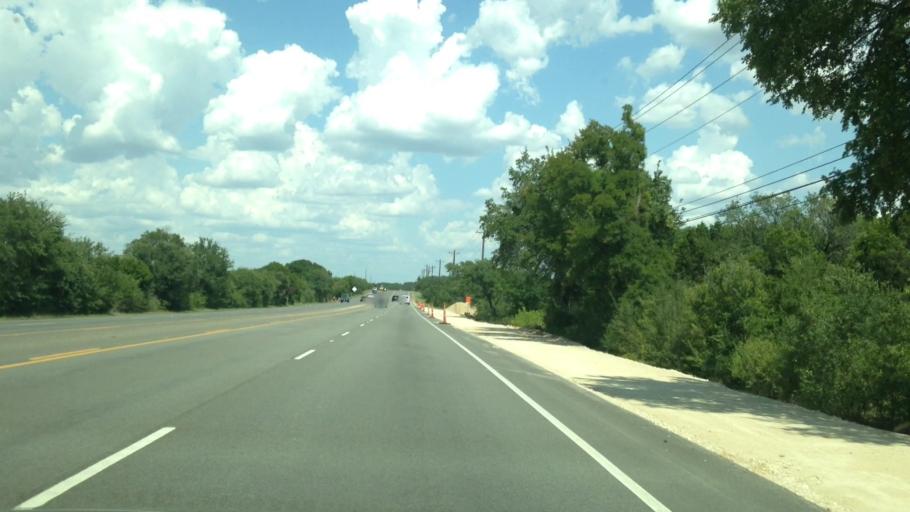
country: US
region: Texas
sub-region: Williamson County
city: Georgetown
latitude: 30.6324
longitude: -97.7371
